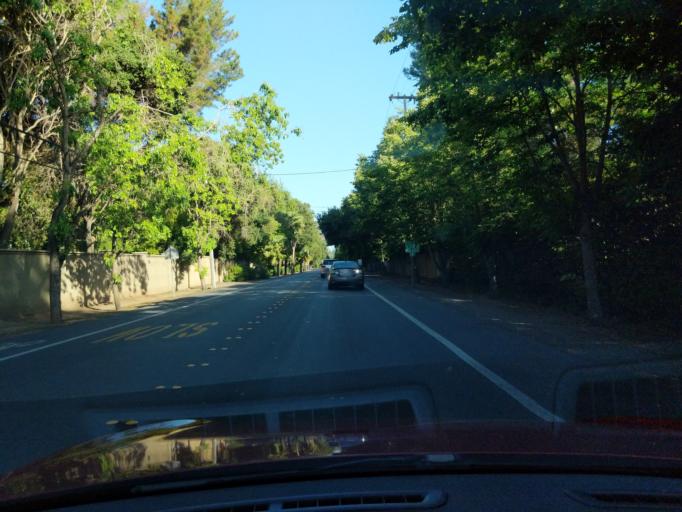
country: US
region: California
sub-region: San Mateo County
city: Menlo Park
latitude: 37.4625
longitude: -122.1796
